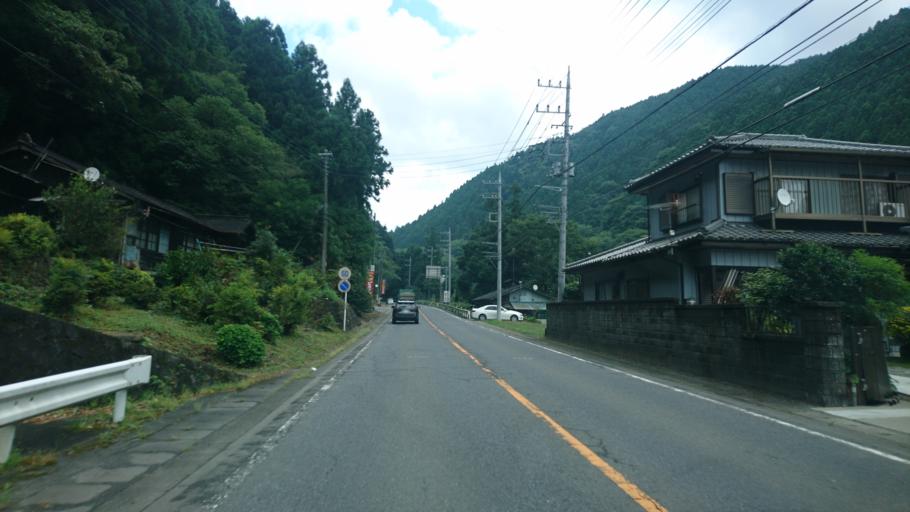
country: JP
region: Gunma
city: Omamacho-omama
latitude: 36.4827
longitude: 139.2608
